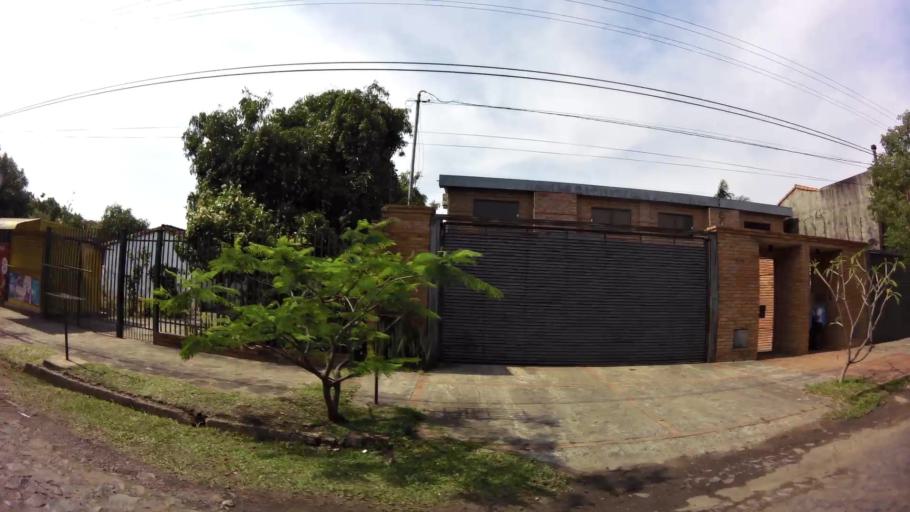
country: PY
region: Central
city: Fernando de la Mora
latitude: -25.2756
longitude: -57.5505
